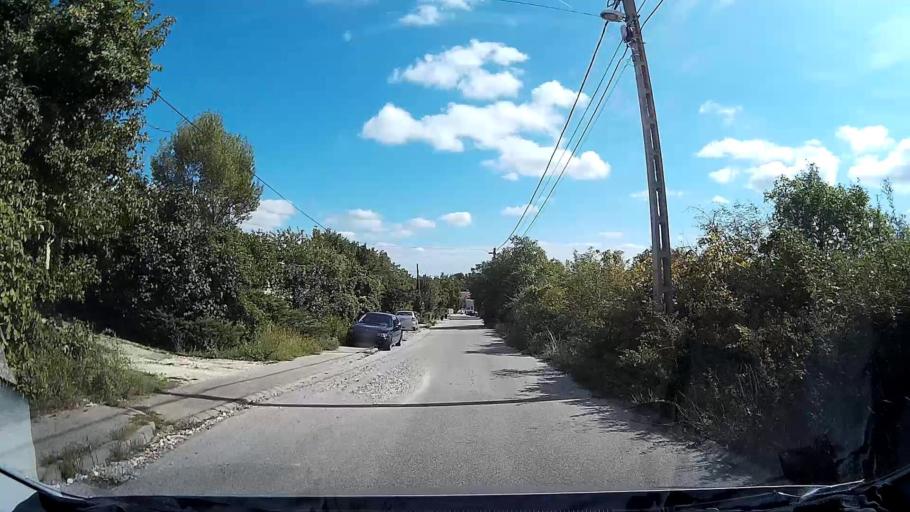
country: HU
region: Pest
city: Szentendre
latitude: 47.6856
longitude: 19.0659
